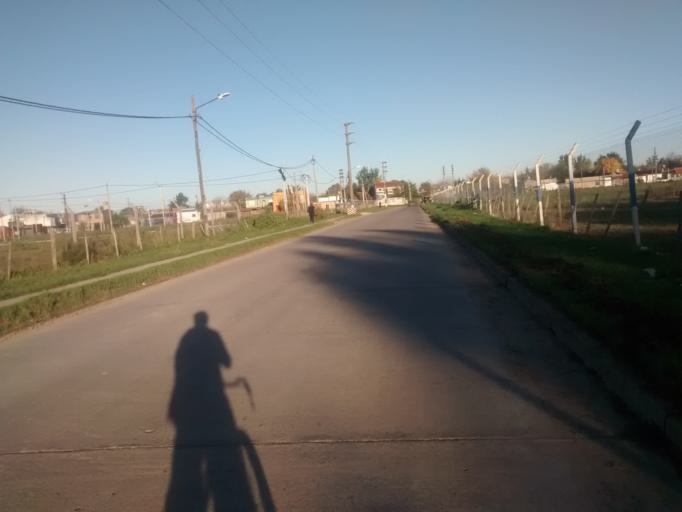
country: AR
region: Buenos Aires
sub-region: Partido de La Plata
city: La Plata
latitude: -34.9037
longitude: -57.9190
